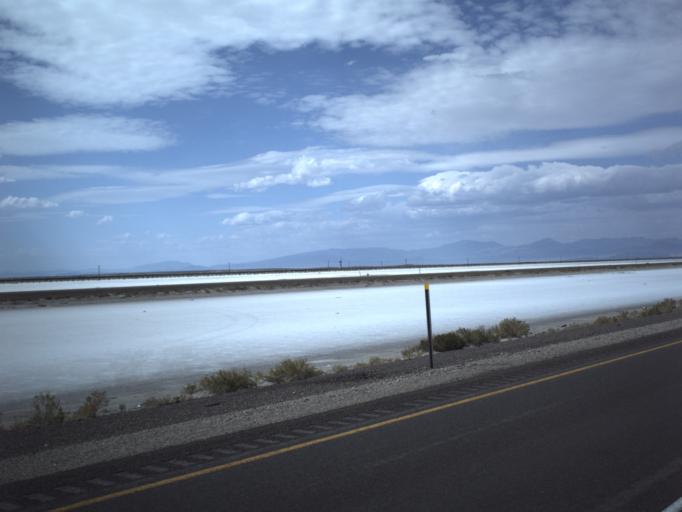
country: US
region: Utah
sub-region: Tooele County
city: Wendover
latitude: 40.7366
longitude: -113.7144
